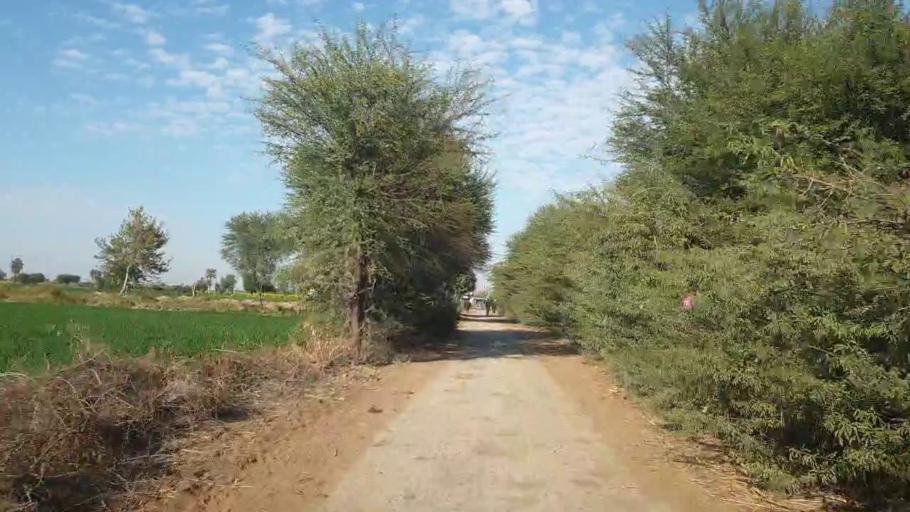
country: PK
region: Sindh
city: Sanghar
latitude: 26.0768
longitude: 68.8749
